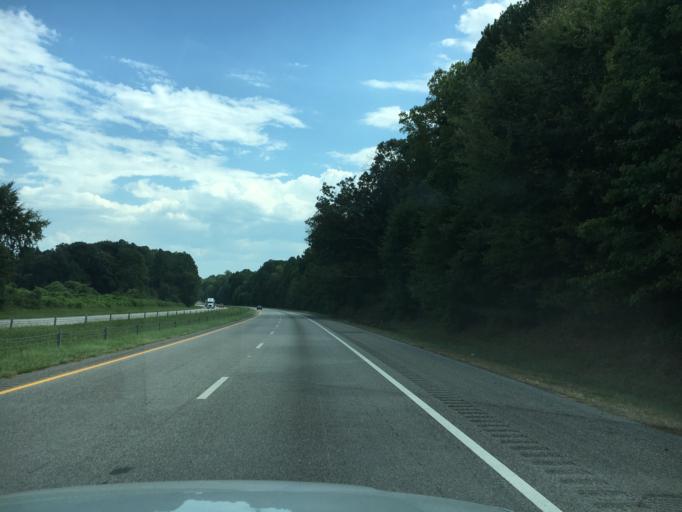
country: US
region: South Carolina
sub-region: Laurens County
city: Clinton
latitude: 34.5312
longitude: -81.8825
